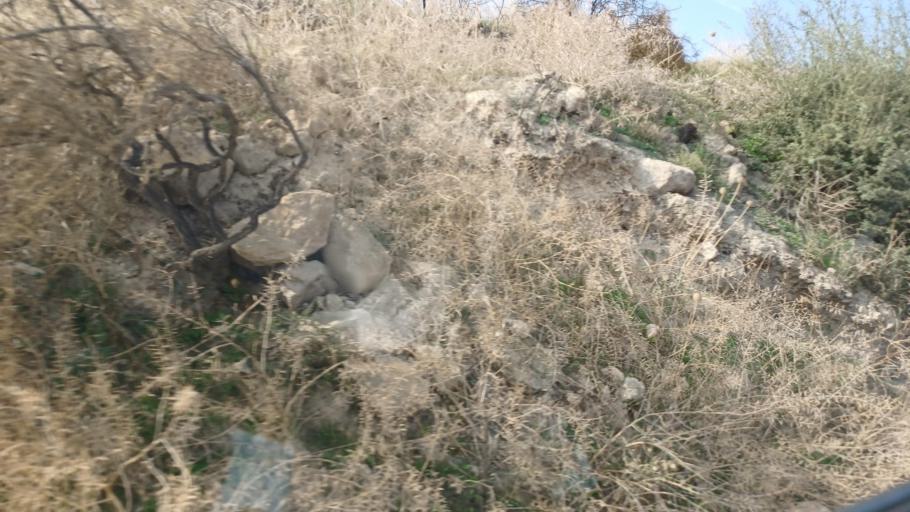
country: CY
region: Pafos
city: Polis
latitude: 34.9738
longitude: 32.4587
